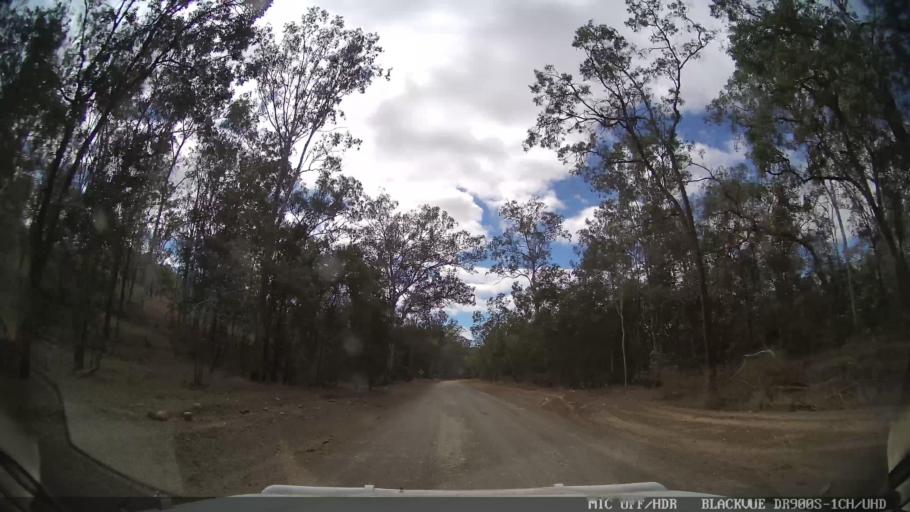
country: AU
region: Queensland
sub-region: Gladstone
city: Toolooa
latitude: -24.5493
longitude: 151.3427
